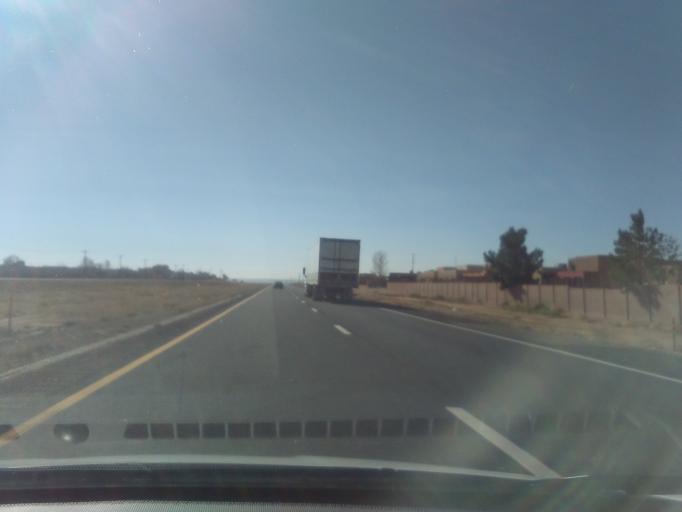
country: US
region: New Mexico
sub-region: Valencia County
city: Los Lunas
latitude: 34.8064
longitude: -106.7648
